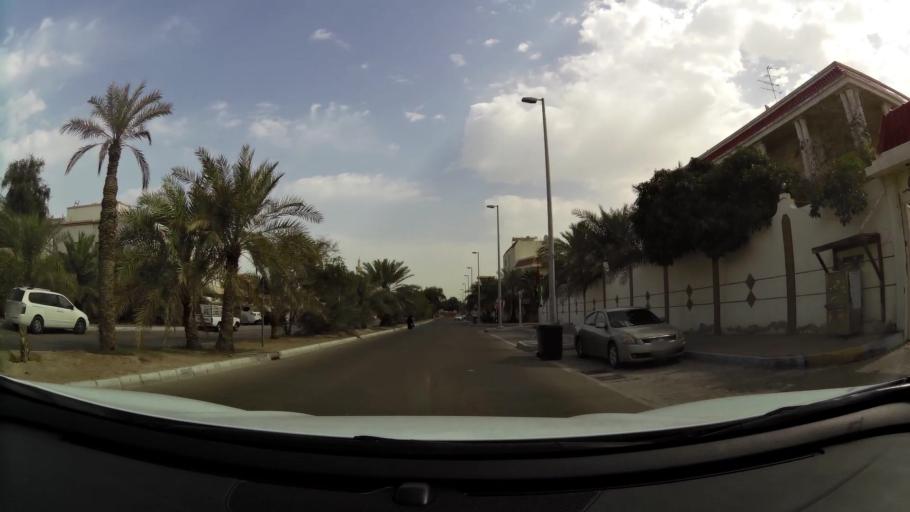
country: AE
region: Abu Dhabi
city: Abu Dhabi
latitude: 24.4424
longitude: 54.3652
